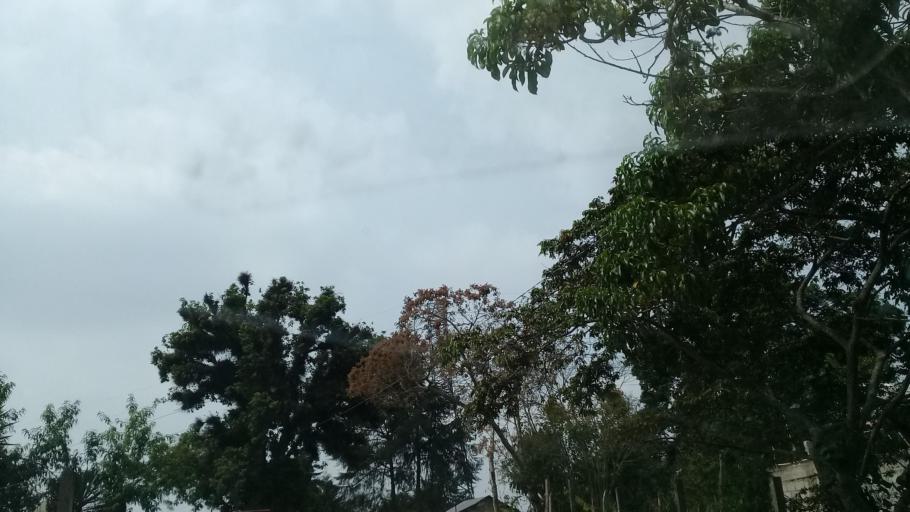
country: MX
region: Veracruz
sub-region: Xalapa
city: Fraccionamiento las Fuentes
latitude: 19.4920
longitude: -96.8985
